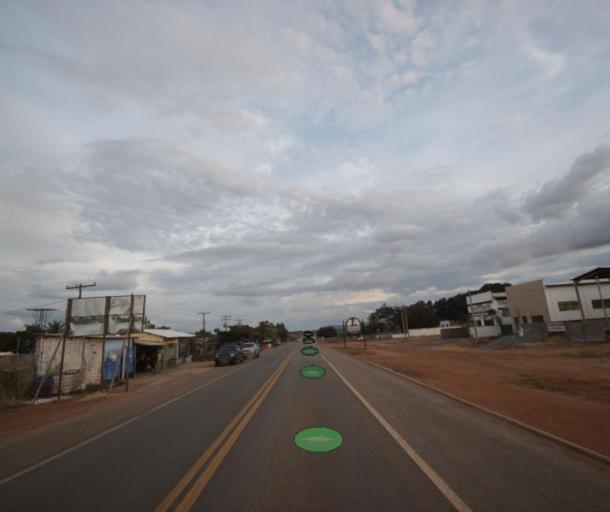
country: BR
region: Goias
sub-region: Barro Alto
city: Barro Alto
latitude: -15.2061
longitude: -48.7005
